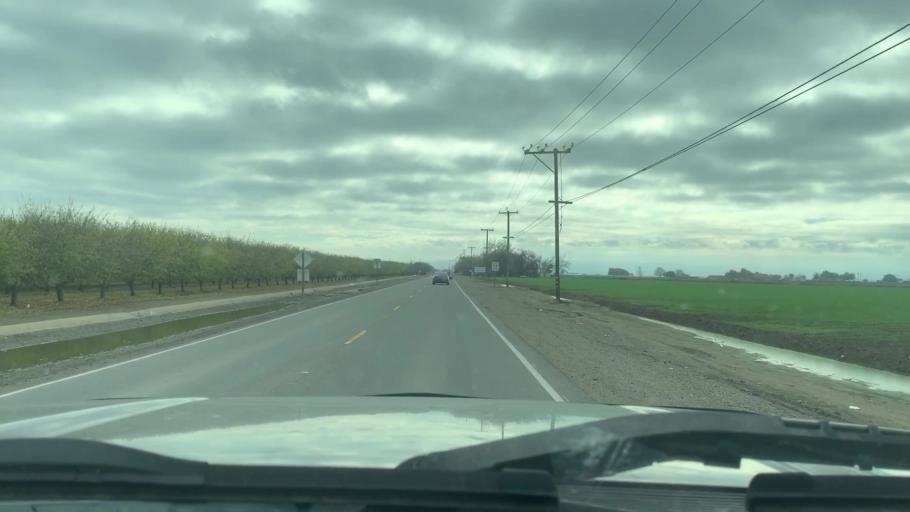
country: US
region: California
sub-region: Merced County
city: Los Banos
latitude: 37.0406
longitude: -120.8358
